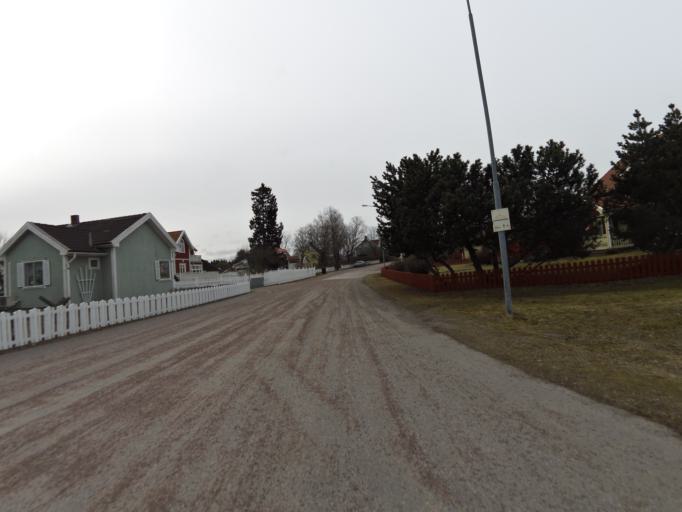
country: SE
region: Gaevleborg
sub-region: Gavle Kommun
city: Gavle
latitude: 60.6563
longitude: 17.1607
